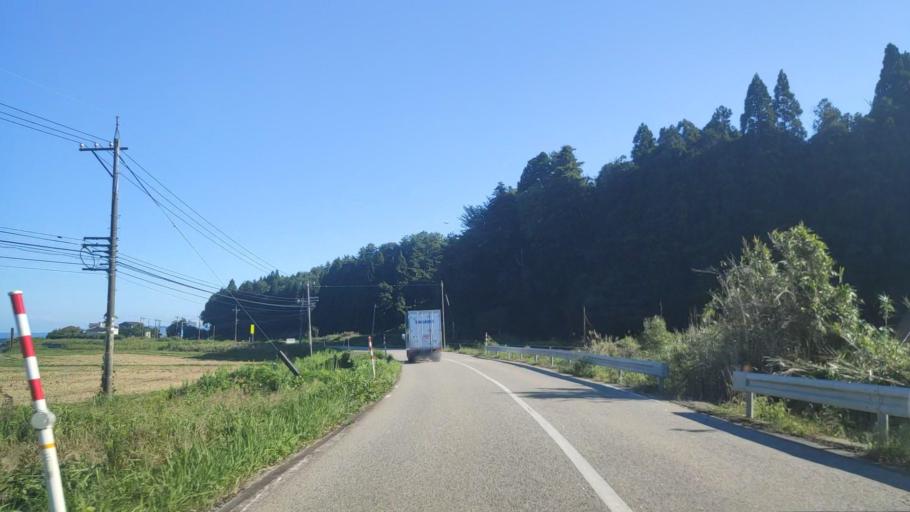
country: JP
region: Ishikawa
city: Nanao
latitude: 37.2016
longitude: 136.9061
